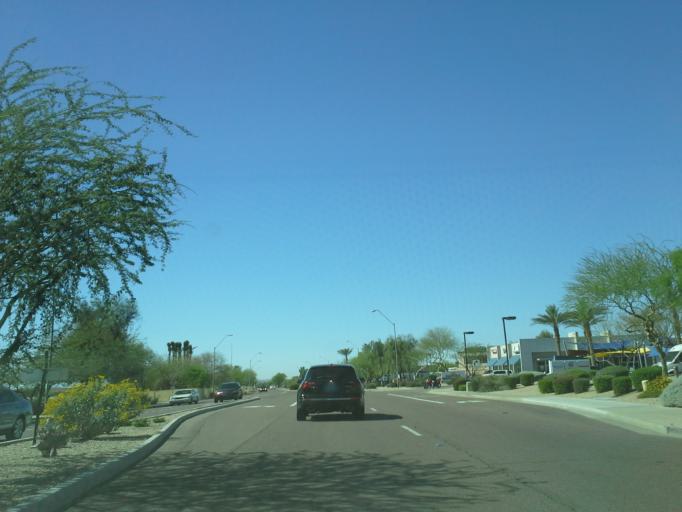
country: US
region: Arizona
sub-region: Maricopa County
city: Paradise Valley
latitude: 33.6269
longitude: -111.8966
